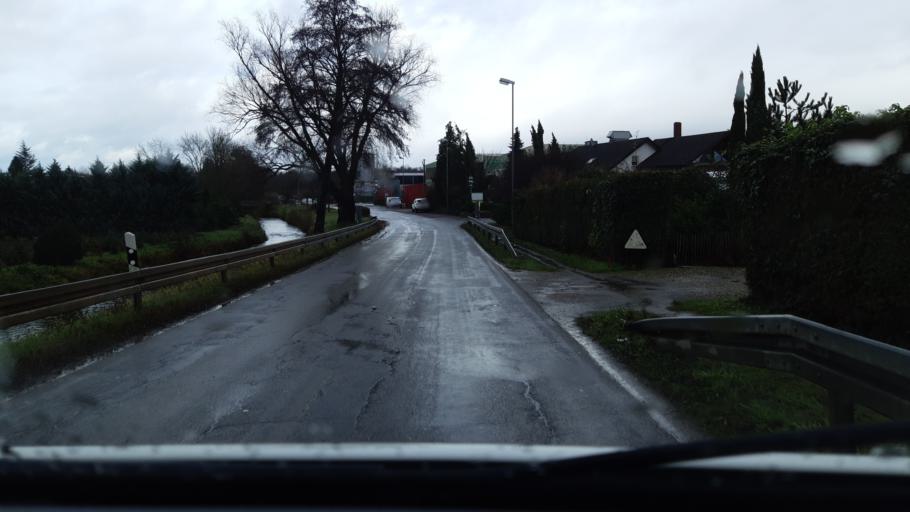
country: DE
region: Baden-Wuerttemberg
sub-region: Freiburg Region
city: Gottenheim
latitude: 48.0520
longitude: 7.7335
